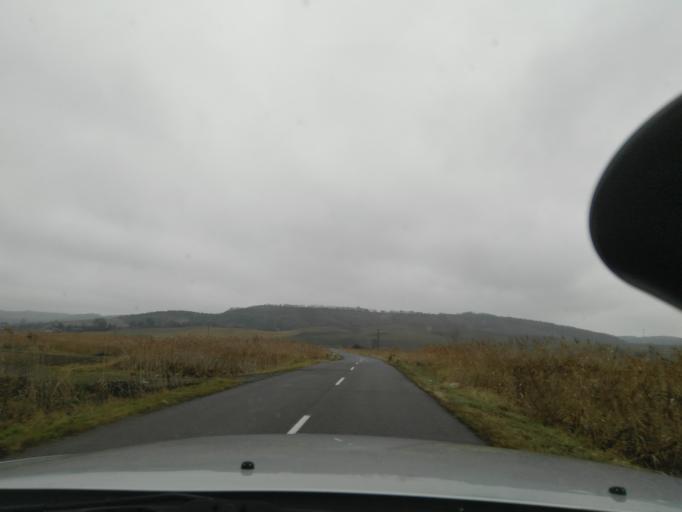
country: HU
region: Nograd
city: Kazar
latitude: 48.0368
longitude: 19.8739
